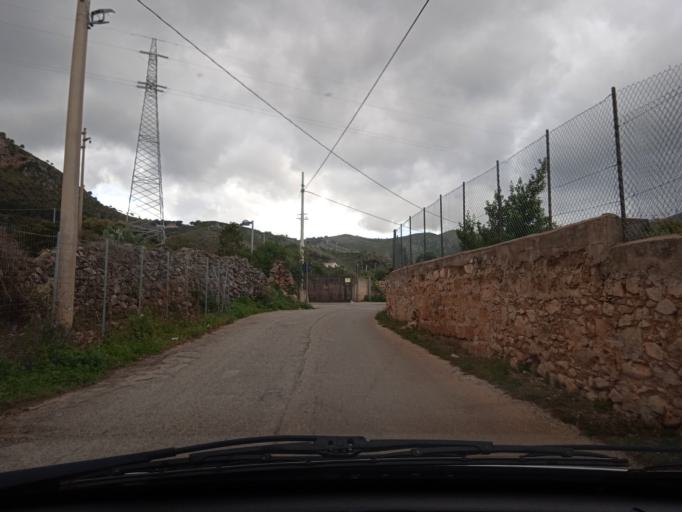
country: IT
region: Sicily
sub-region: Palermo
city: Villabate
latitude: 38.0725
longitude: 13.4381
